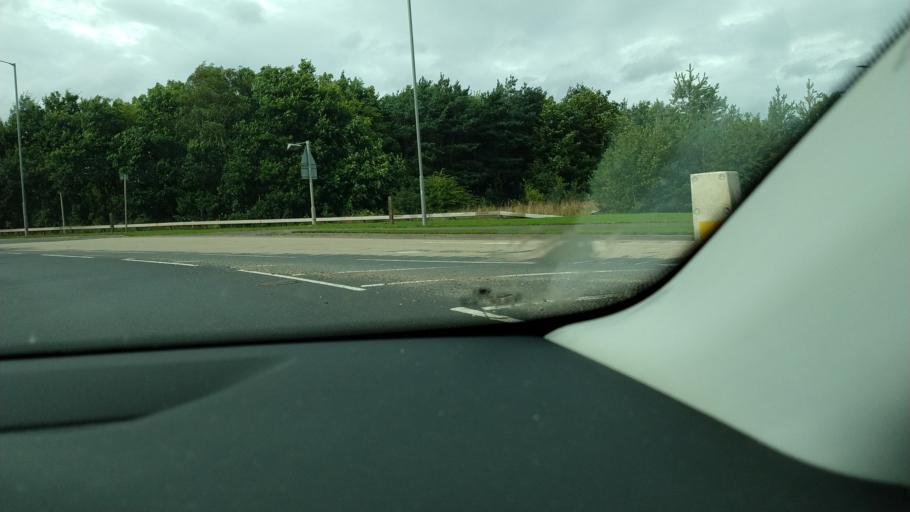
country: GB
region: England
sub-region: East Riding of Yorkshire
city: Airmyn
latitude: 53.7054
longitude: -0.9087
